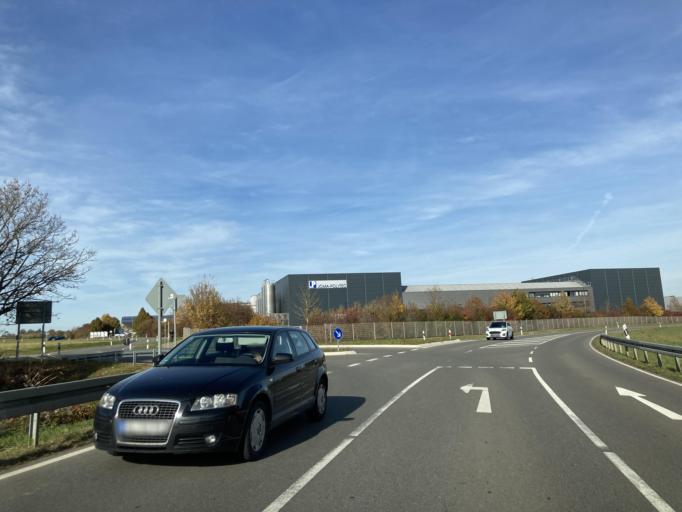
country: DE
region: Baden-Wuerttemberg
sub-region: Tuebingen Region
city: Bodelshausen
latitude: 48.3811
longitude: 8.9594
